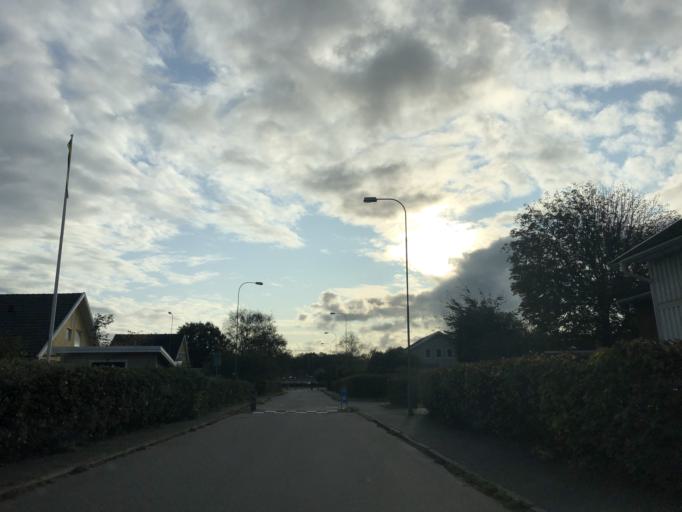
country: SE
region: Vaestra Goetaland
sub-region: Goteborg
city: Majorna
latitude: 57.6632
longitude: 11.8828
